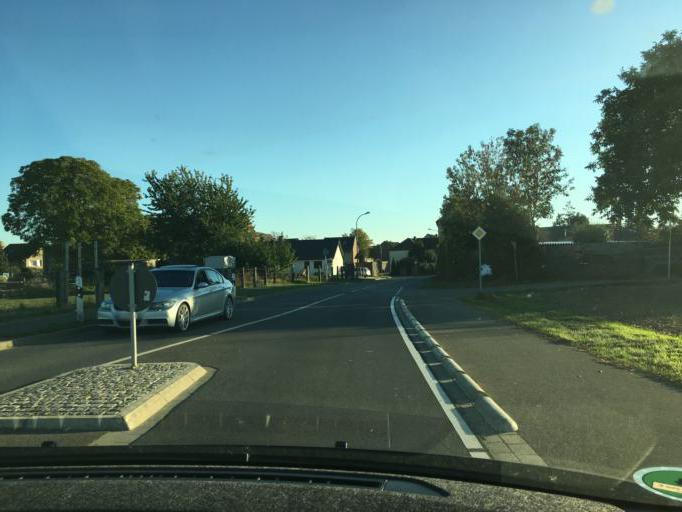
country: DE
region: North Rhine-Westphalia
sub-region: Regierungsbezirk Koln
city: Inden
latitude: 50.8299
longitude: 6.4169
